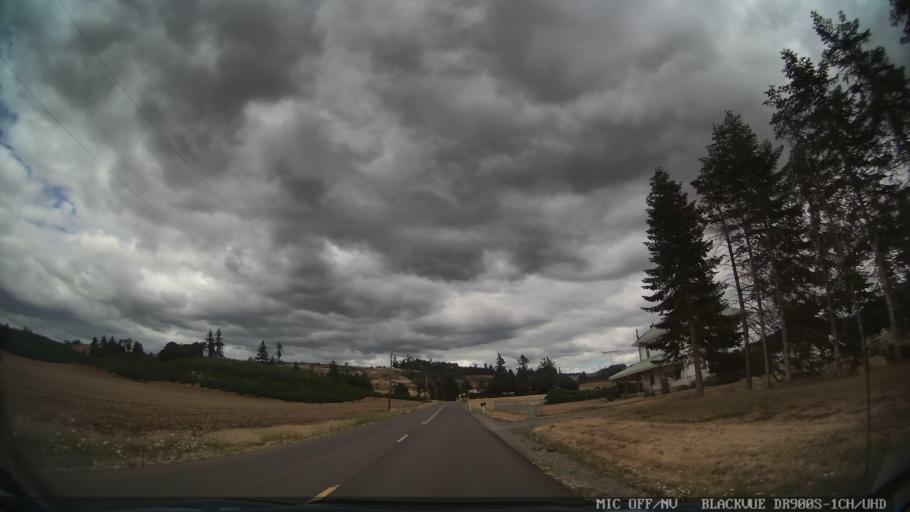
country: US
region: Oregon
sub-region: Marion County
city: Sublimity
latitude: 44.8725
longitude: -122.7121
